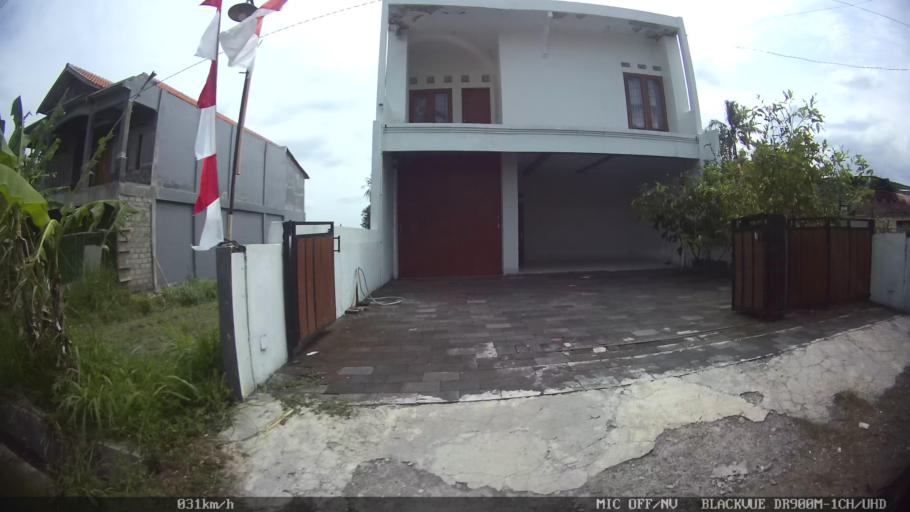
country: ID
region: Central Java
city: Candi Prambanan
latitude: -7.7354
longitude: 110.4785
